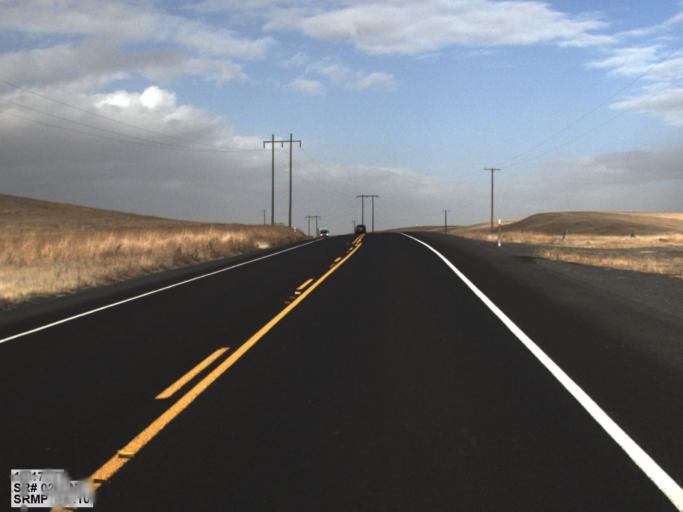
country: US
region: Washington
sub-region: Lincoln County
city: Davenport
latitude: 47.5305
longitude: -118.2016
